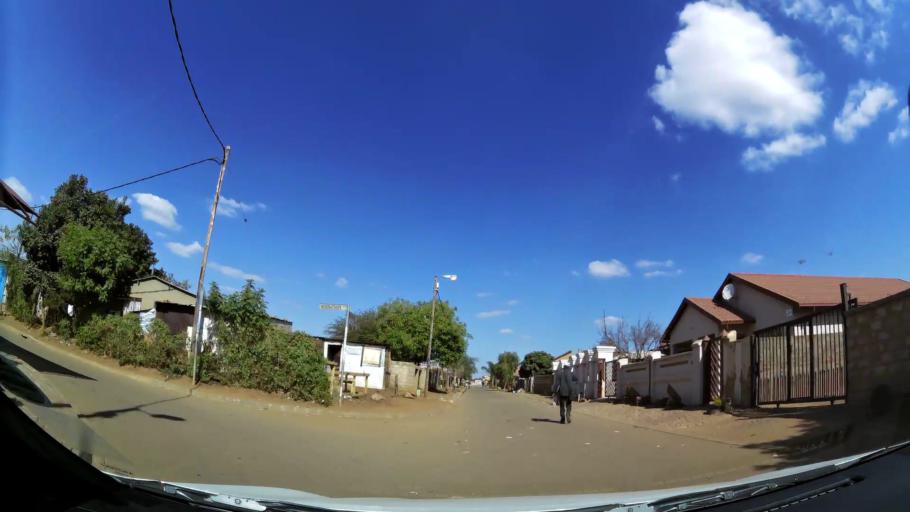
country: ZA
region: Gauteng
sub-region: City of Tshwane Metropolitan Municipality
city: Cullinan
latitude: -25.7180
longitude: 28.4060
